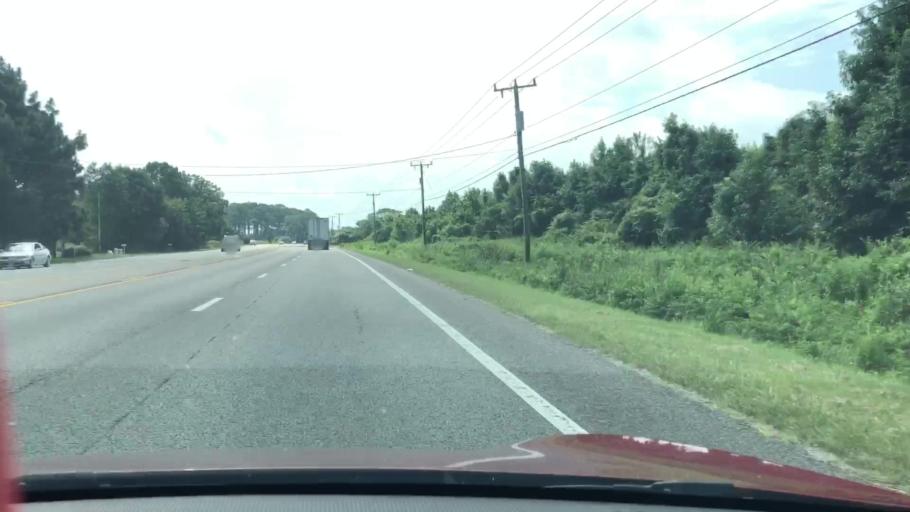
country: US
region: North Carolina
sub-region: Dare County
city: Southern Shores
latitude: 36.2169
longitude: -75.8680
